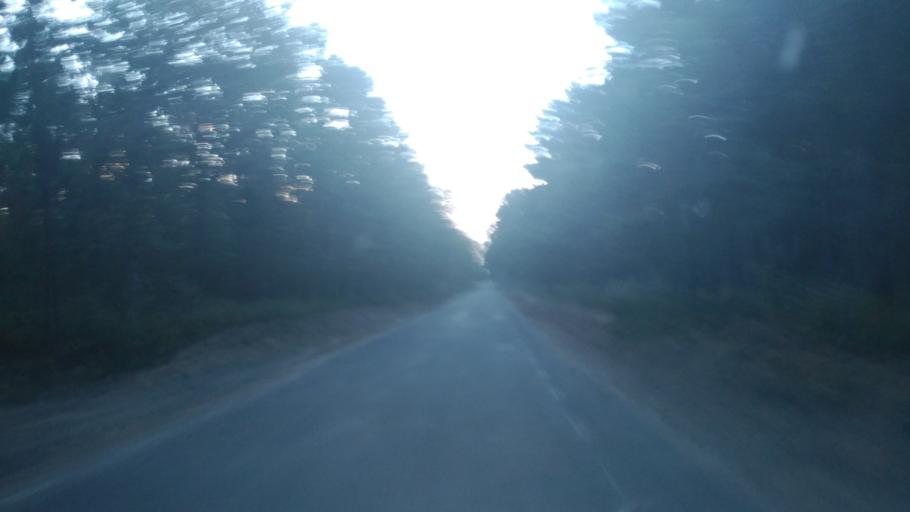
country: ES
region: Castille and Leon
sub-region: Provincia de Salamanca
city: Nava de Francia
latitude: 40.5251
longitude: -6.1332
